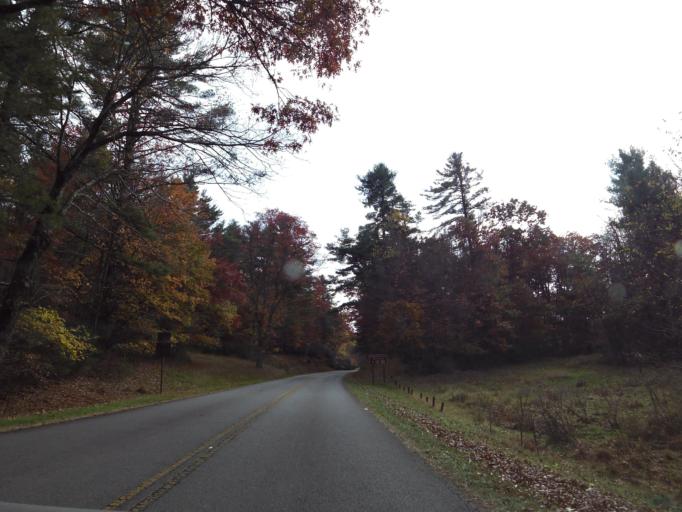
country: US
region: Virginia
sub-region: City of Galax
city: Galax
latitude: 36.5560
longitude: -80.9084
